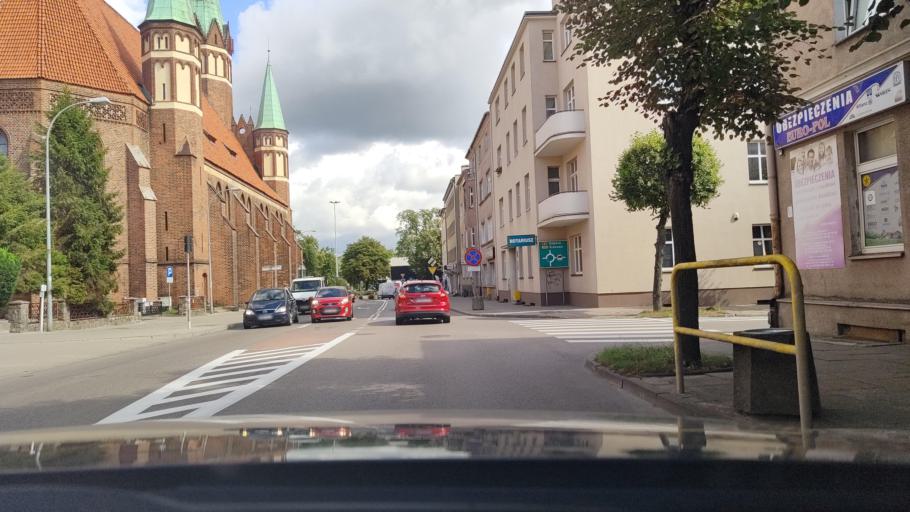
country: PL
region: Pomeranian Voivodeship
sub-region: Powiat wejherowski
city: Wejherowo
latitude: 54.6016
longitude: 18.2337
